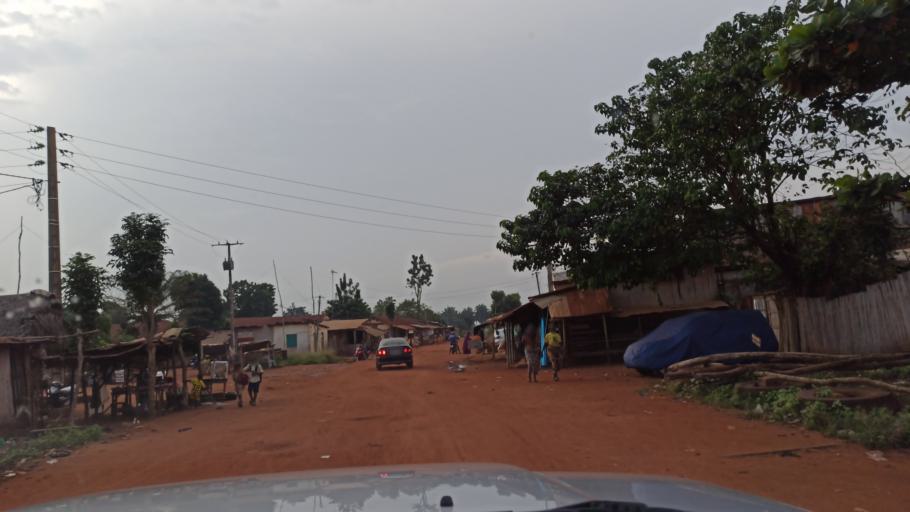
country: BJ
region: Queme
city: Porto-Novo
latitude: 6.5334
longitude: 2.6595
